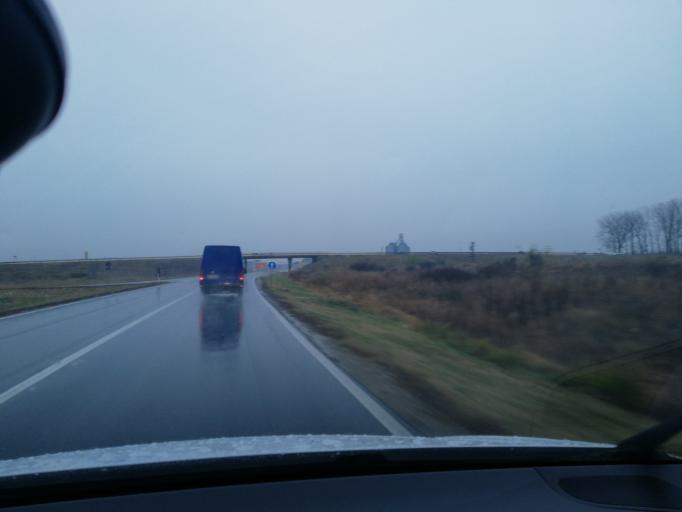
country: RS
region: Autonomna Pokrajina Vojvodina
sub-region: Sremski Okrug
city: Ruma
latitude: 45.0098
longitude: 19.8474
